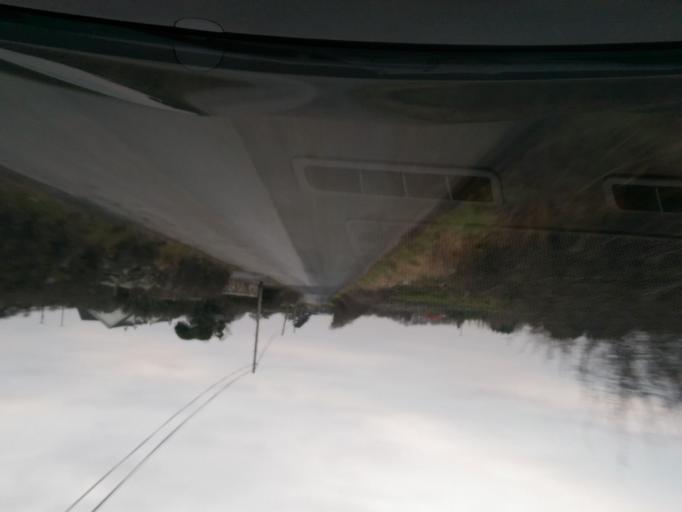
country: IE
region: Connaught
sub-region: County Galway
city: Bearna
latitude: 53.2655
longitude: -9.1553
